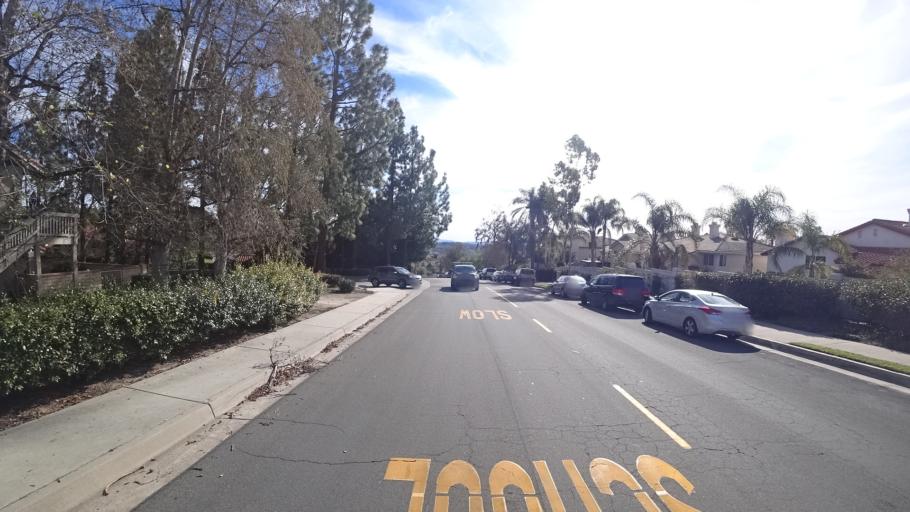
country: US
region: California
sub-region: Orange County
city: Portola Hills
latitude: 33.6861
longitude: -117.6274
